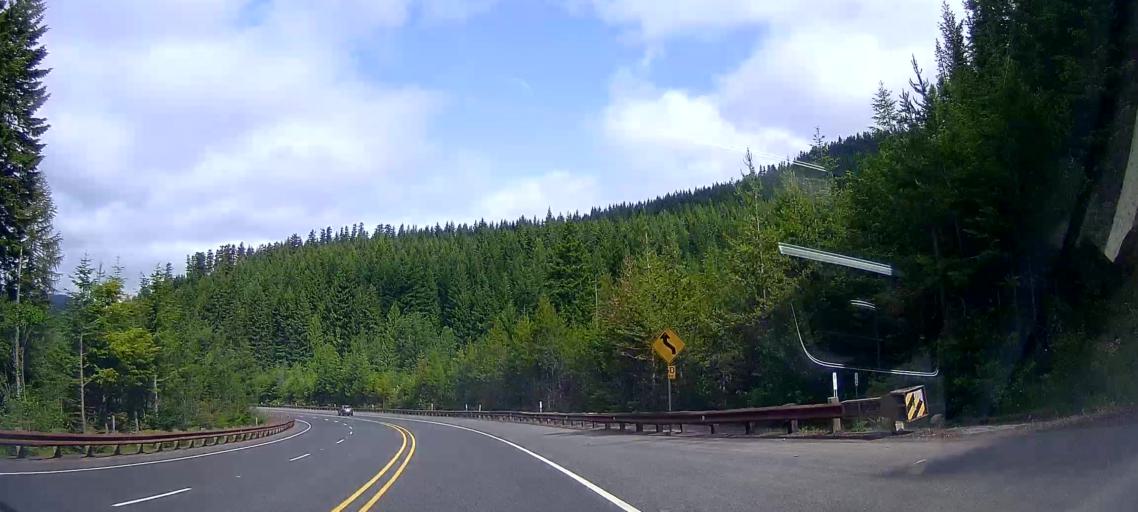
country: US
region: Oregon
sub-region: Clackamas County
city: Mount Hood Village
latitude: 45.2404
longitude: -121.6997
